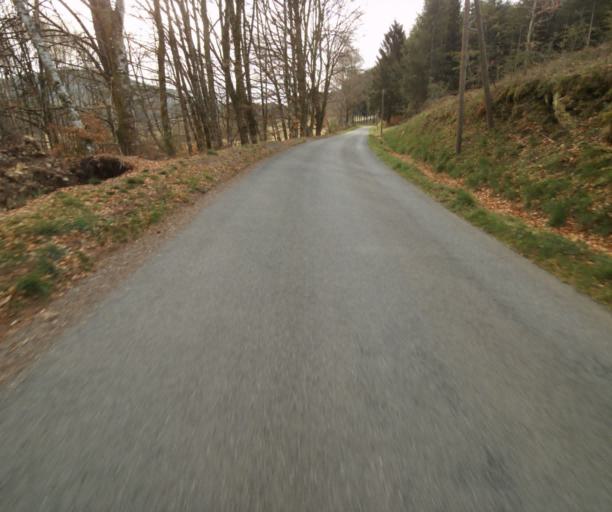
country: FR
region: Limousin
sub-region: Departement de la Correze
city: Treignac
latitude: 45.4693
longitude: 1.8040
